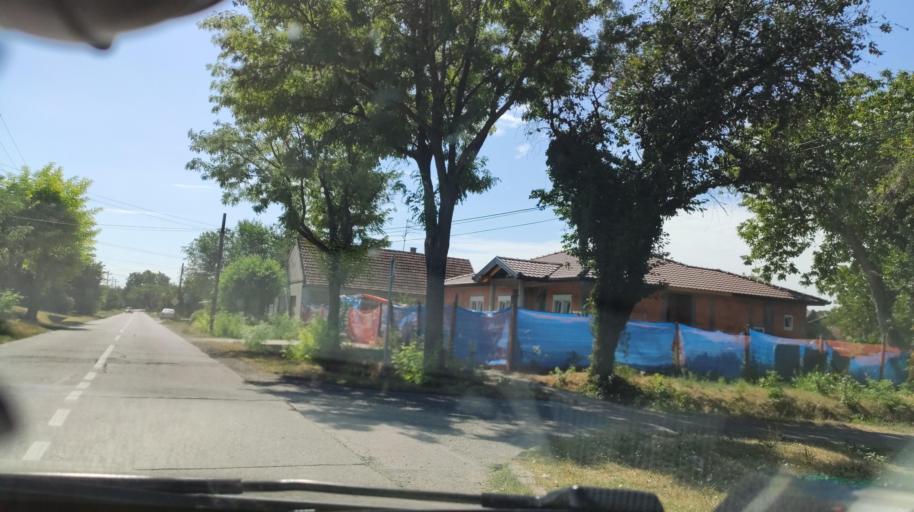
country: RS
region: Autonomna Pokrajina Vojvodina
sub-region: Severnobacki Okrug
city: Backa Topola
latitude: 45.8088
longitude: 19.6244
